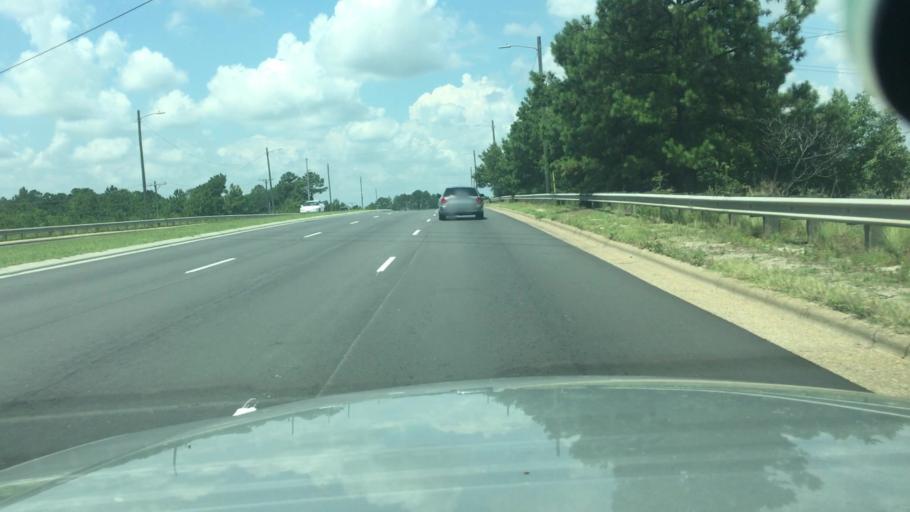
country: US
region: North Carolina
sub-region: Cumberland County
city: Fayetteville
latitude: 35.0200
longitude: -78.9171
